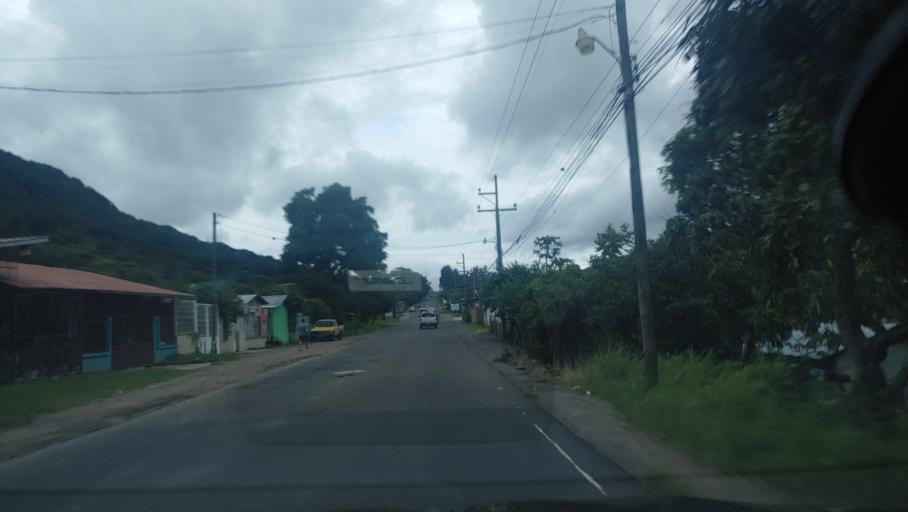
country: HN
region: Choluteca
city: San Marcos de Colon
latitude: 13.3757
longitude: -86.9002
